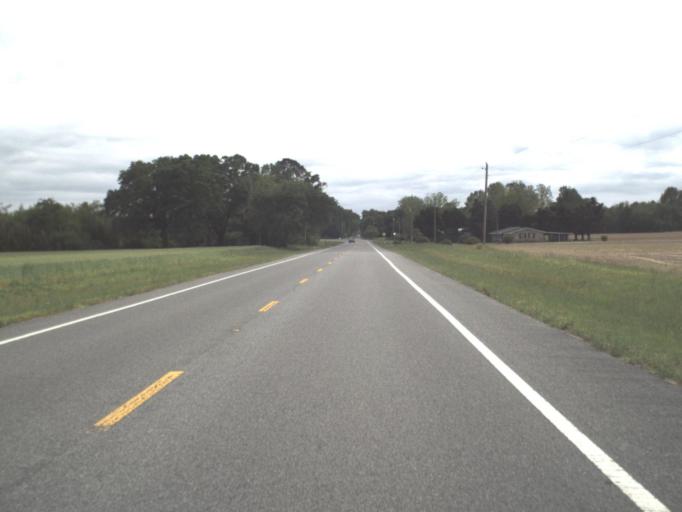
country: US
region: Florida
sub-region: Santa Rosa County
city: Point Baker
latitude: 30.7090
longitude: -87.0785
